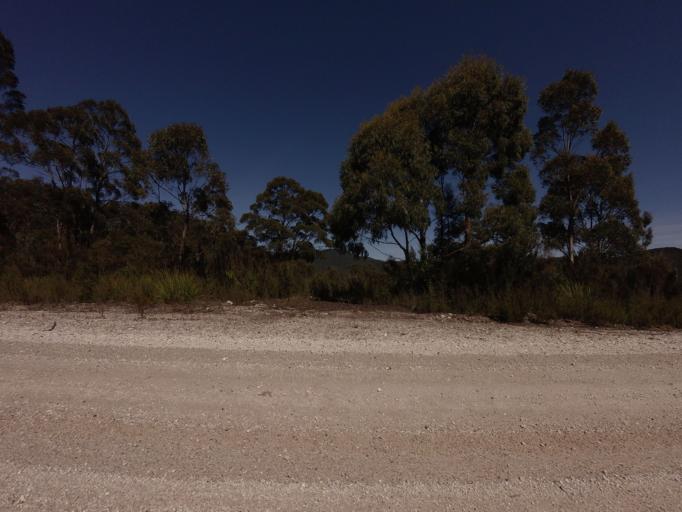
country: AU
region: Tasmania
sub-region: Huon Valley
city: Geeveston
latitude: -42.9123
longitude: 146.3618
